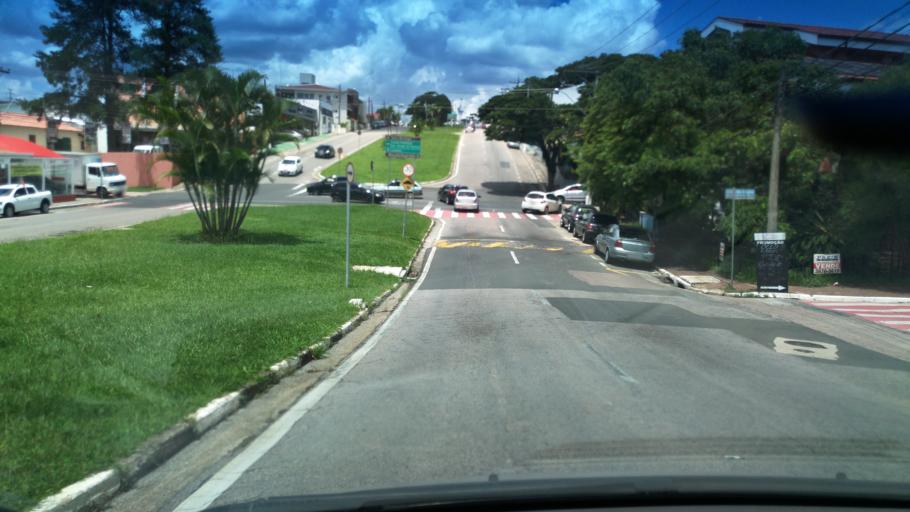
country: BR
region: Sao Paulo
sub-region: Vinhedo
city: Vinhedo
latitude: -23.0318
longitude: -46.9801
